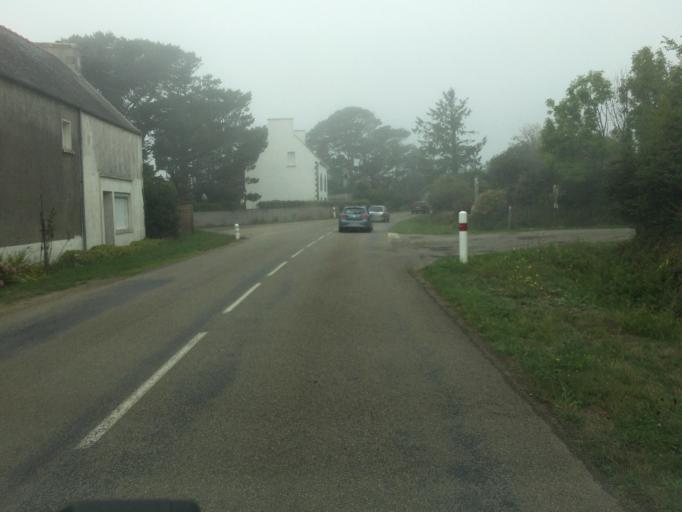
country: FR
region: Brittany
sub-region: Departement du Finistere
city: Plogoff
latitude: 48.0570
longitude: -4.6961
